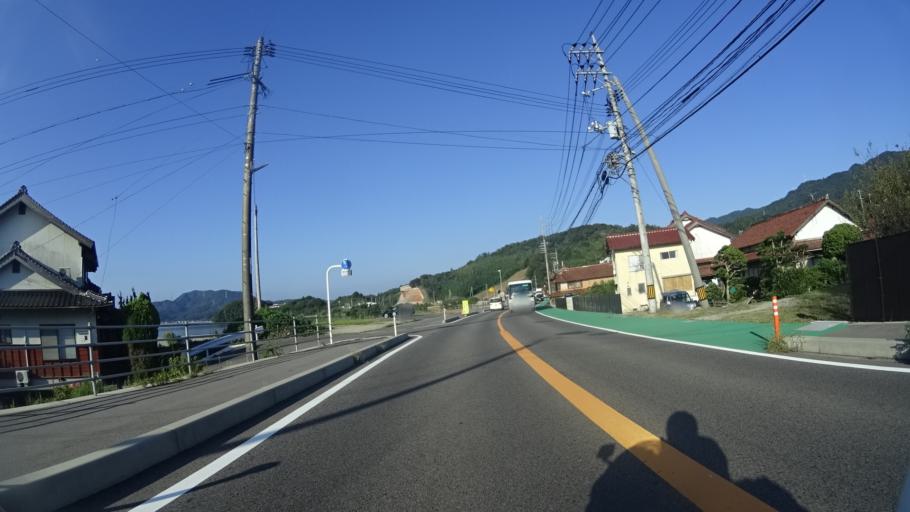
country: JP
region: Shimane
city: Sakaiminato
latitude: 35.5208
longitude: 133.1431
